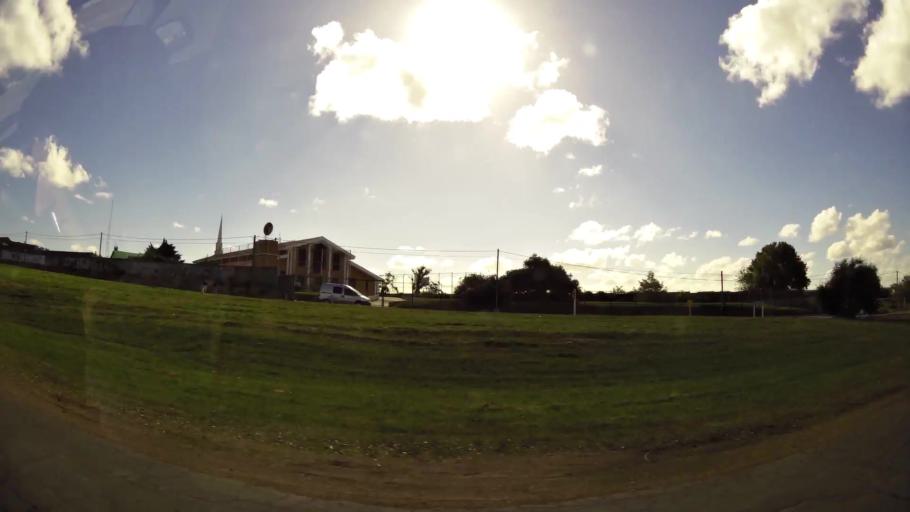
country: UY
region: Canelones
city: La Paz
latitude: -34.8421
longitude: -56.2540
